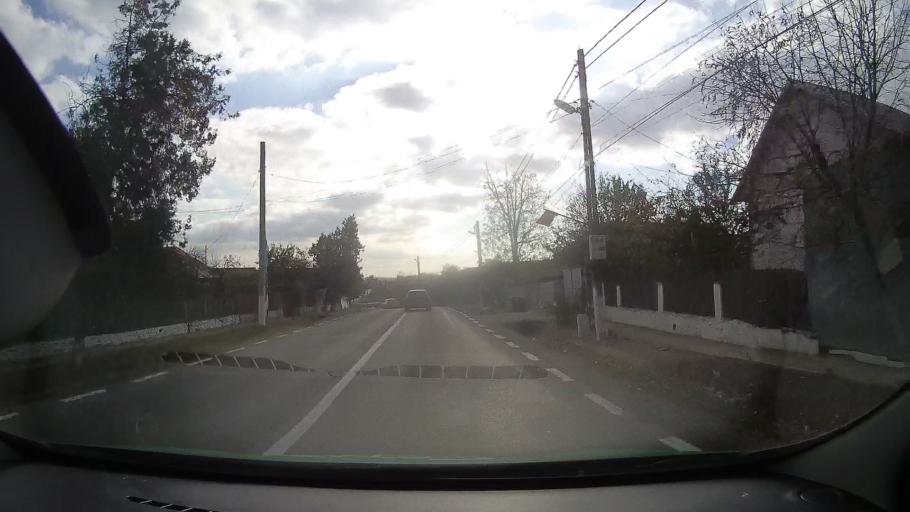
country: RO
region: Tulcea
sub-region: Comuna Topolog
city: Topolog
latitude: 44.8767
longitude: 28.3743
